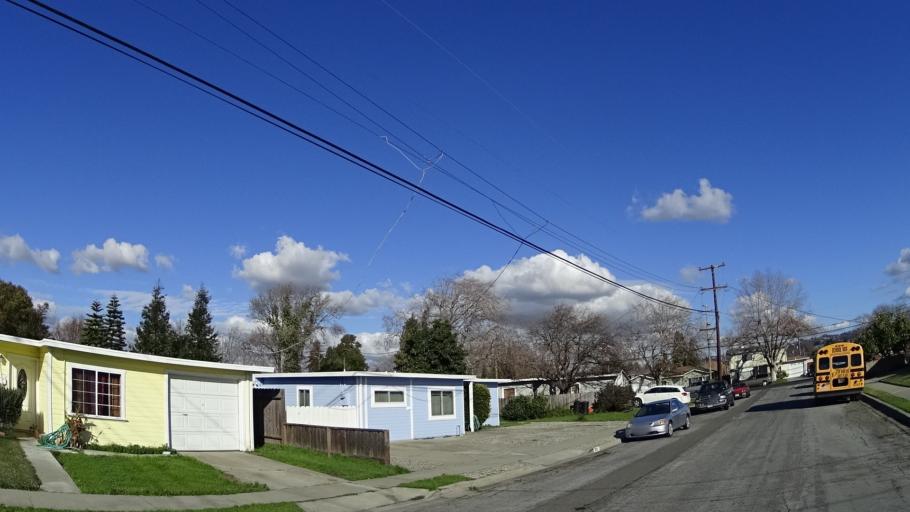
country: US
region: California
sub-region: Alameda County
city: Cherryland
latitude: 37.6616
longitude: -122.1028
